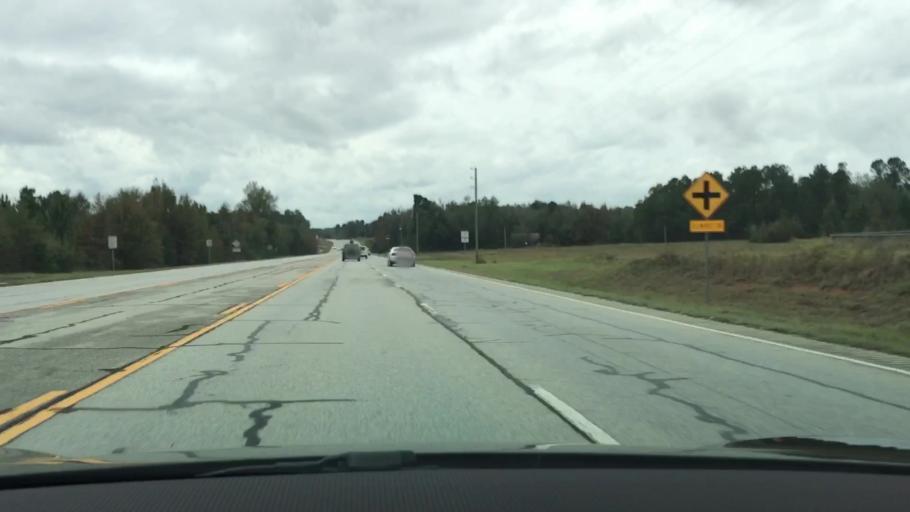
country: US
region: Georgia
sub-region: Jefferson County
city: Wadley
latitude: 32.8815
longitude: -82.3959
